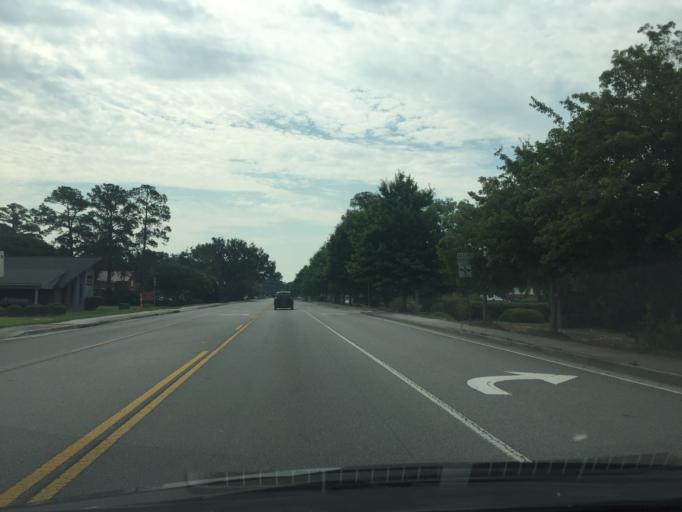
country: US
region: Georgia
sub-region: Chatham County
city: Isle of Hope
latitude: 32.0115
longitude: -81.1051
